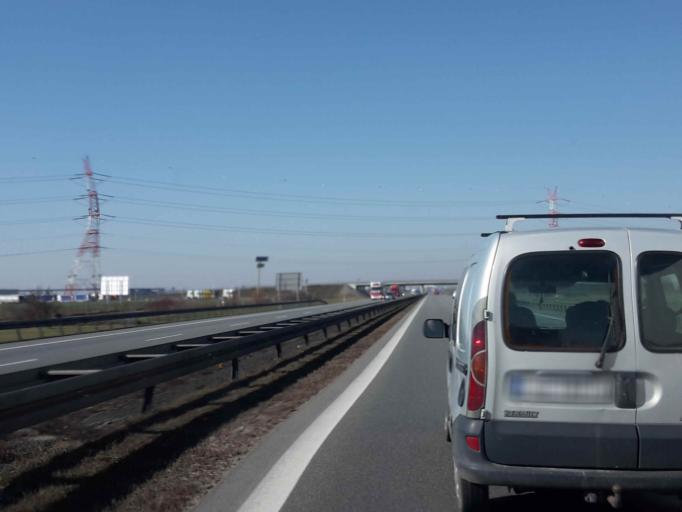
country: PL
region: Greater Poland Voivodeship
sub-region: Powiat poznanski
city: Komorniki
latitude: 52.3503
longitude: 16.8106
